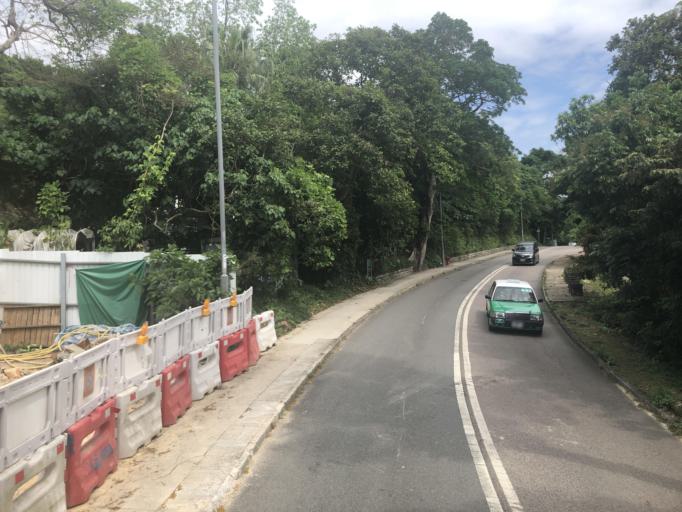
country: HK
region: Sai Kung
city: Sai Kung
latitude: 22.3964
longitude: 114.2863
